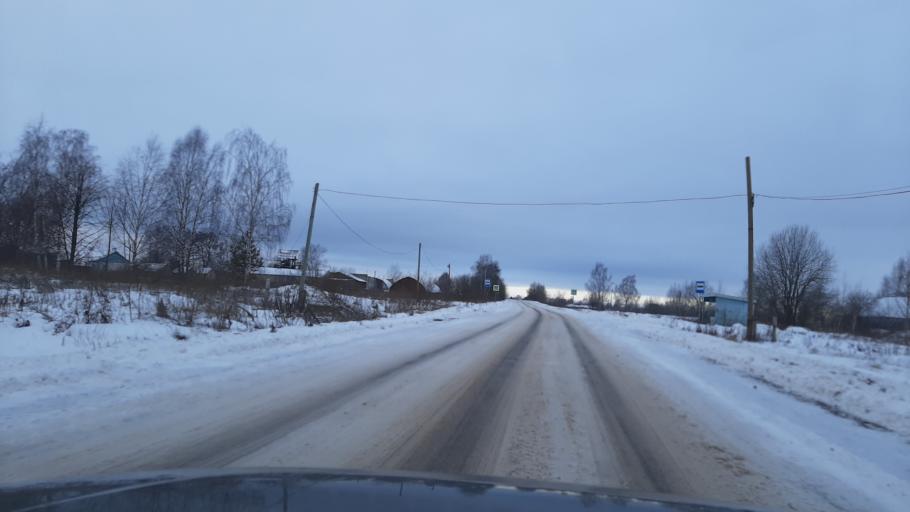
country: RU
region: Kostroma
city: Volgorechensk
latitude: 57.4343
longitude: 41.0678
